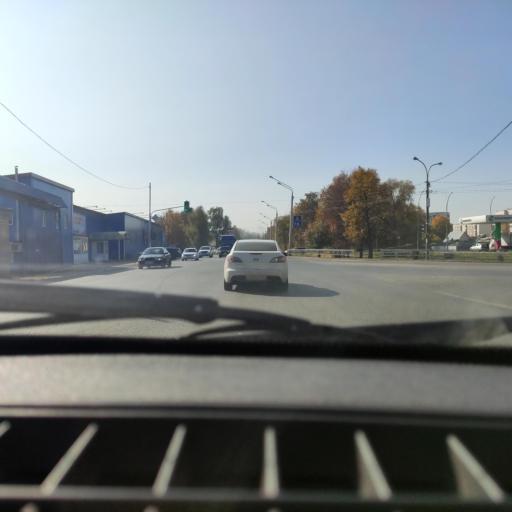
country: RU
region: Bashkortostan
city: Avdon
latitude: 54.6956
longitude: 55.8282
